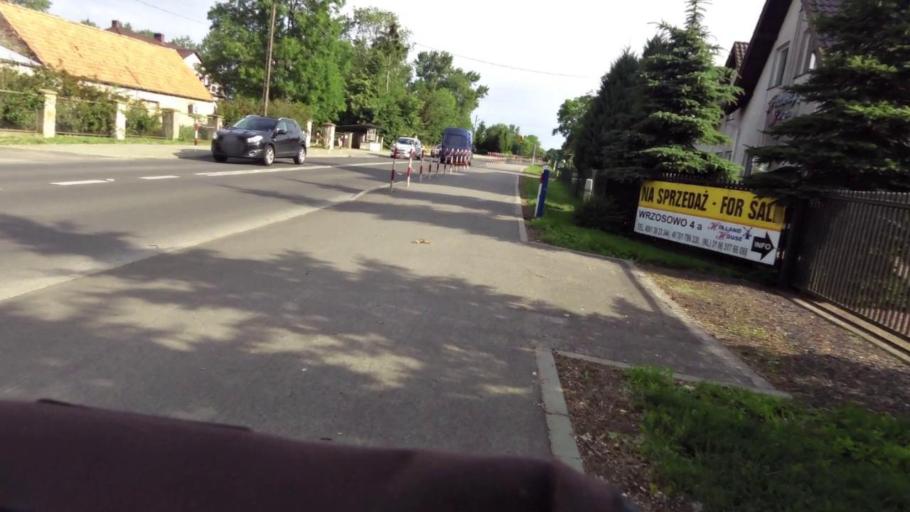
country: PL
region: West Pomeranian Voivodeship
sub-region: Powiat kamienski
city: Kamien Pomorski
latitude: 53.9979
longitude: 14.8171
